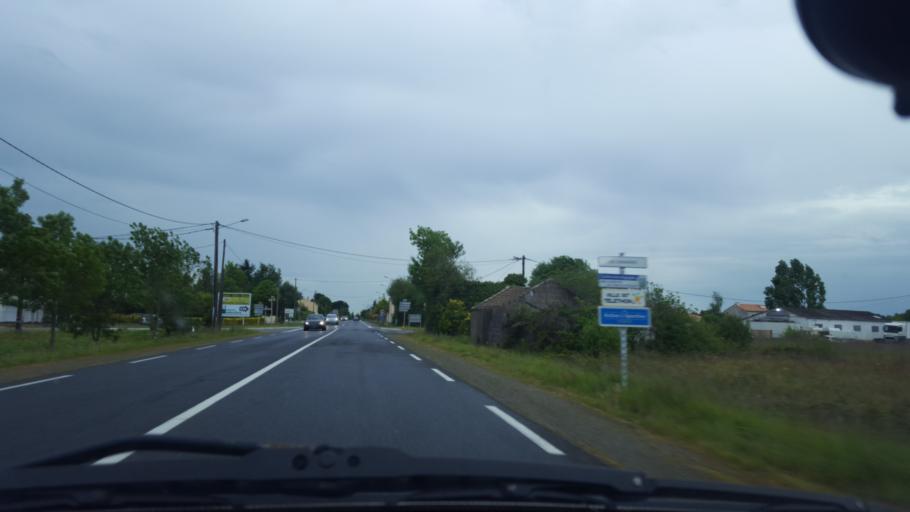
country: FR
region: Pays de la Loire
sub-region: Departement de la Loire-Atlantique
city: Les Sorinieres
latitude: 47.1398
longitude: -1.5204
